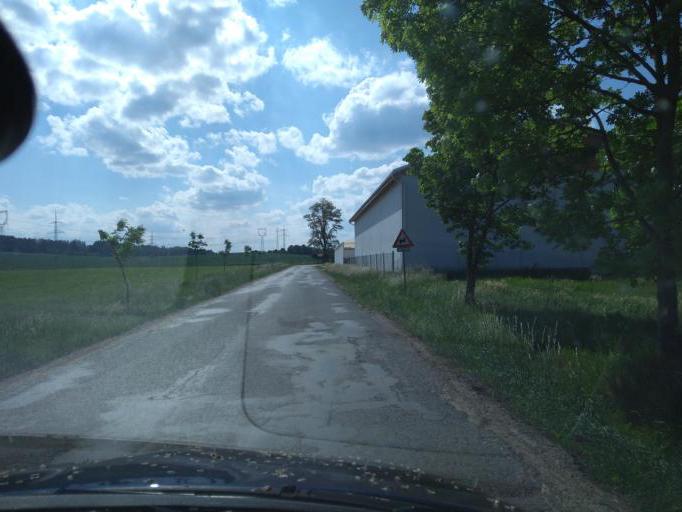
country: CZ
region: Plzensky
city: Merklin
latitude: 49.5956
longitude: 13.2475
